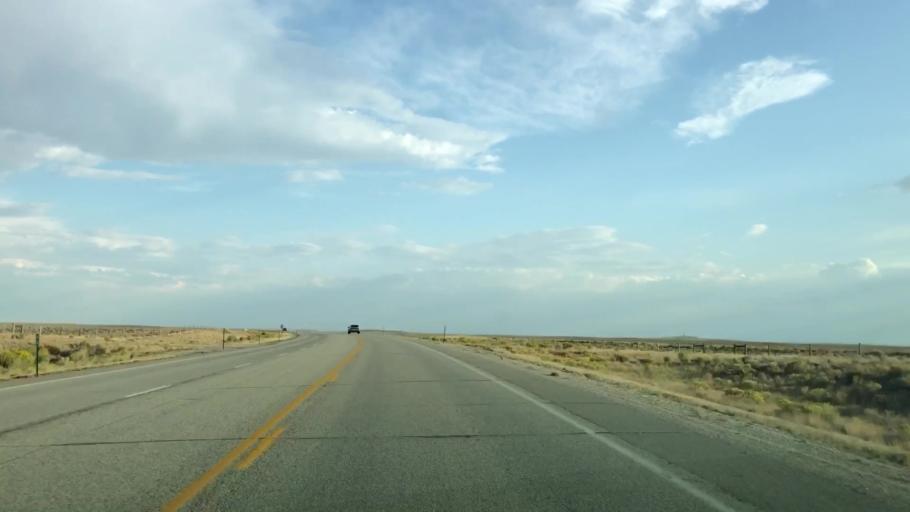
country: US
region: Wyoming
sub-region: Sublette County
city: Pinedale
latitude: 42.4146
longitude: -109.5542
